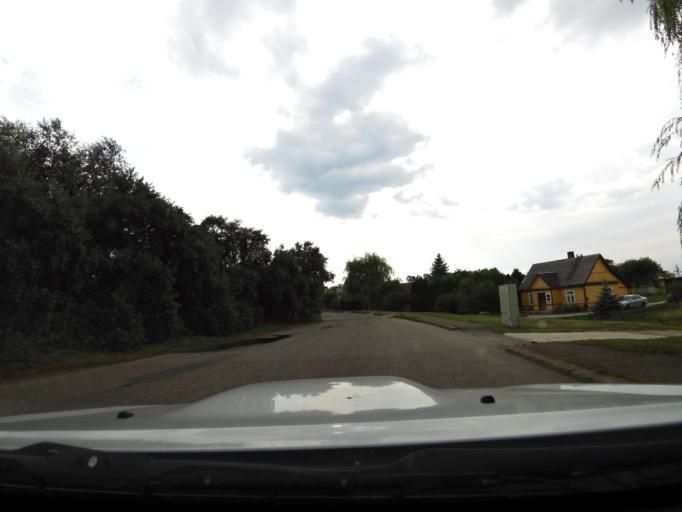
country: LT
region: Vilnius County
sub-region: Vilniaus Rajonas
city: Vievis
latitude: 54.7772
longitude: 24.8249
